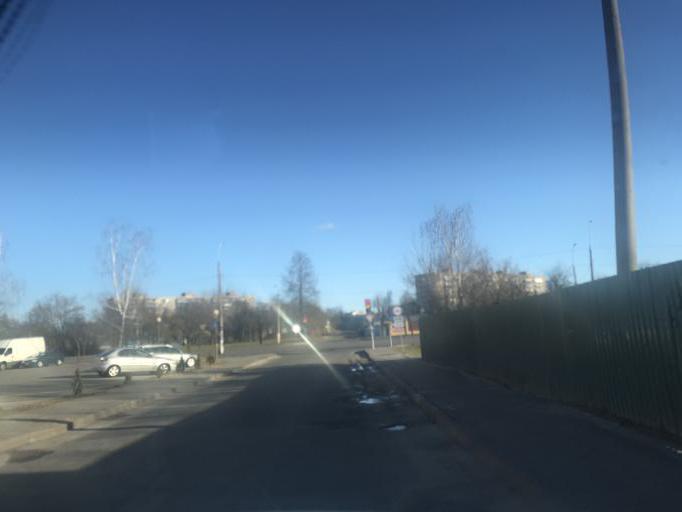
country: BY
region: Mogilev
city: Mahilyow
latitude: 53.9095
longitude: 30.3572
